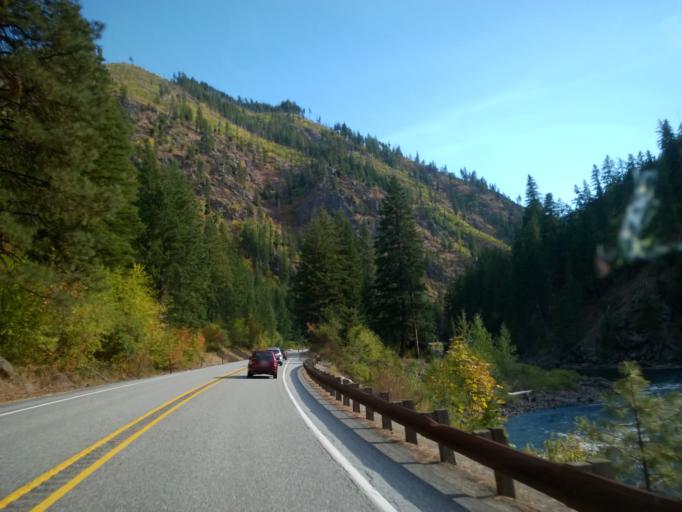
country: US
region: Washington
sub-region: Chelan County
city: Leavenworth
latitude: 47.6426
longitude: -120.7210
